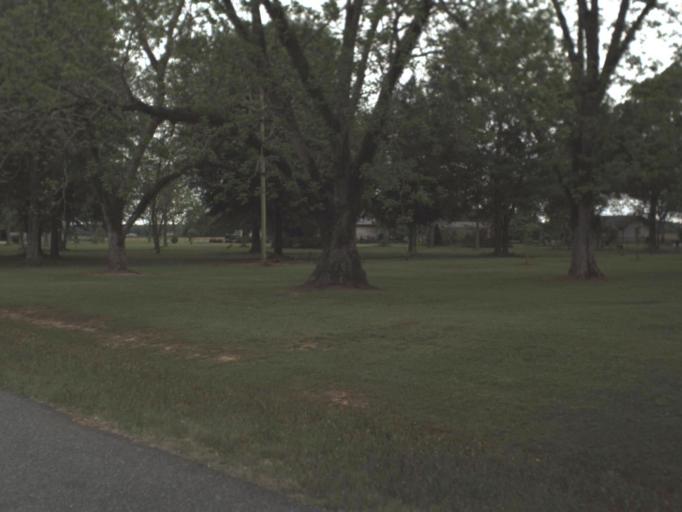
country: US
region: Florida
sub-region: Santa Rosa County
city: Point Baker
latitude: 30.7715
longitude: -87.0420
